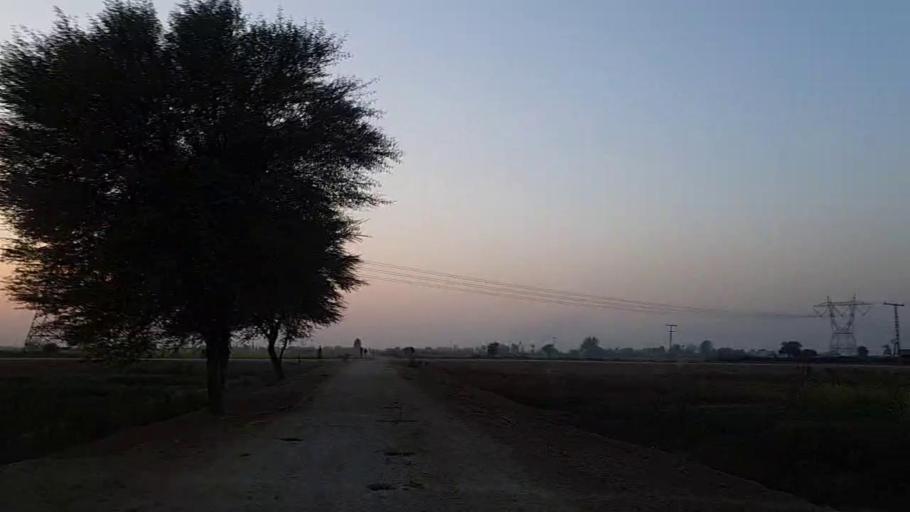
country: PK
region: Sindh
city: Hala
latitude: 25.9402
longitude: 68.4488
